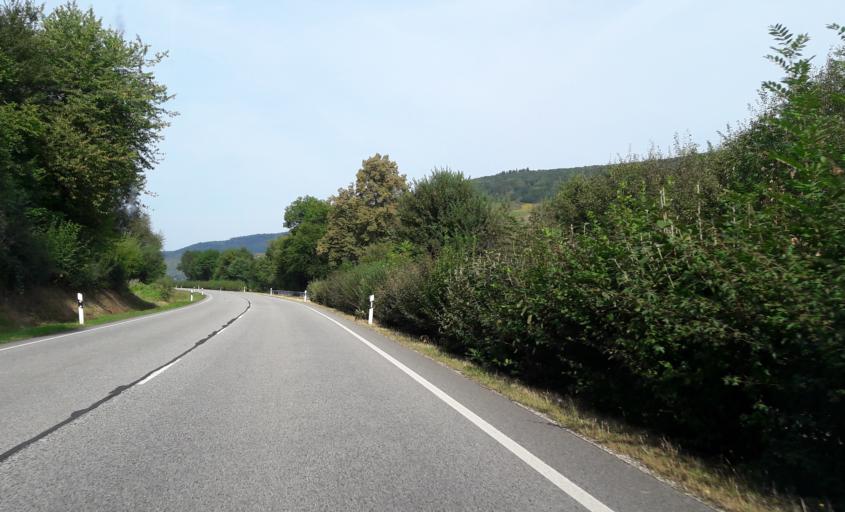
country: DE
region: Rheinland-Pfalz
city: Zell
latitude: 50.0367
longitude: 7.1672
